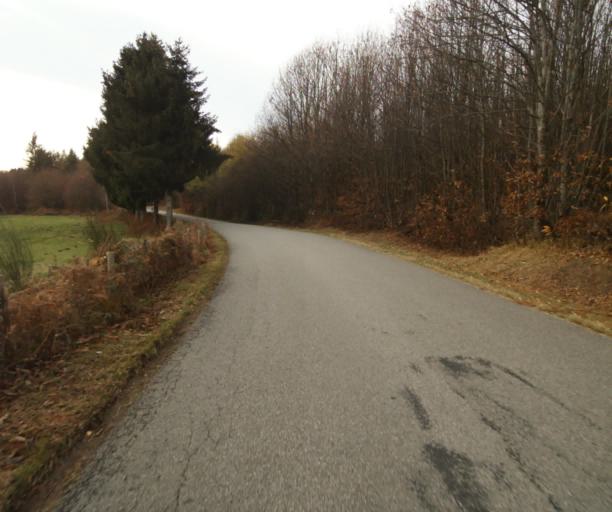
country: FR
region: Limousin
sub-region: Departement de la Correze
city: Sainte-Fortunade
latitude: 45.1802
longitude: 1.7506
